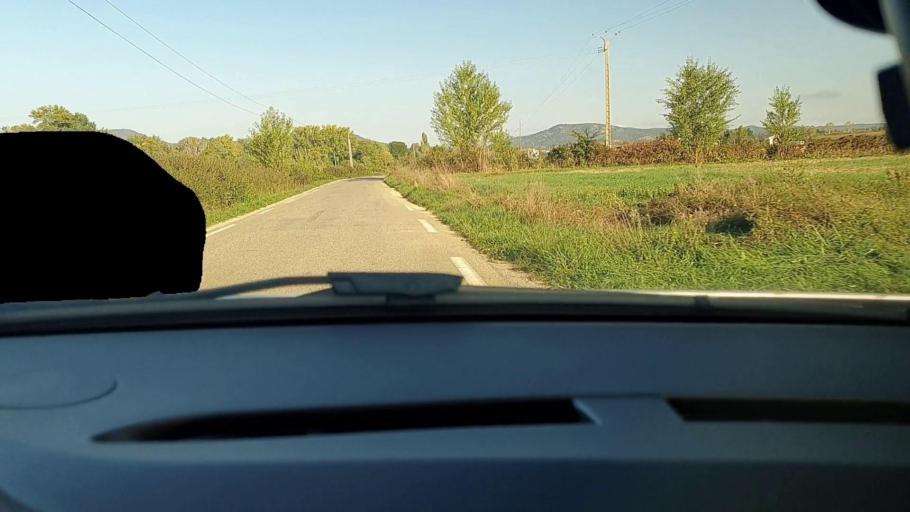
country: FR
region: Languedoc-Roussillon
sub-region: Departement du Gard
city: Saint-Ambroix
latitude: 44.2650
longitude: 4.2791
